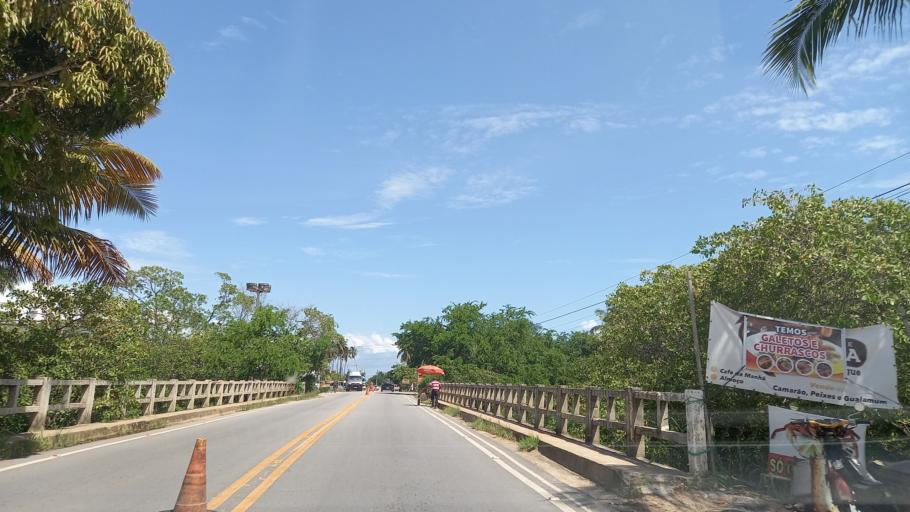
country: BR
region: Pernambuco
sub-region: Sao Jose Da Coroa Grande
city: Sao Jose da Coroa Grande
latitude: -8.9134
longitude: -35.1540
